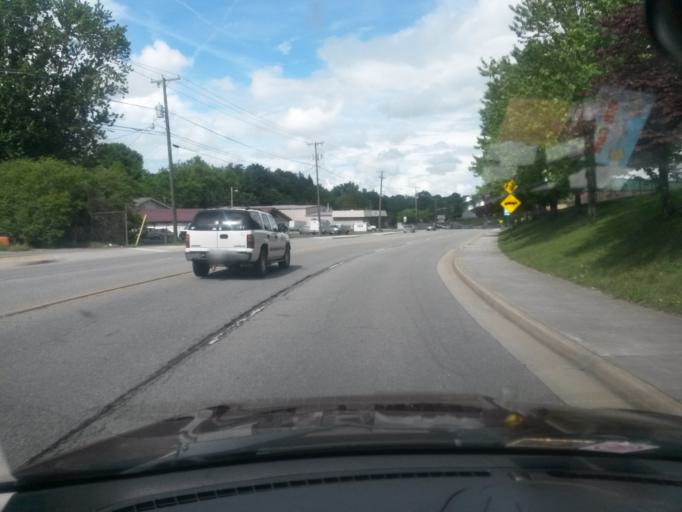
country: US
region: Virginia
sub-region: Montgomery County
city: Christiansburg
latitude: 37.1296
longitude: -80.4161
